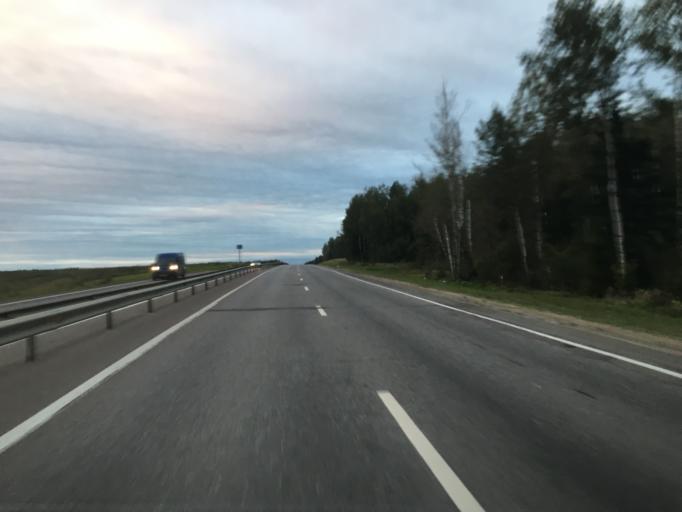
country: RU
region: Kaluga
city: Kaluga
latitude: 54.6482
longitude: 36.2931
